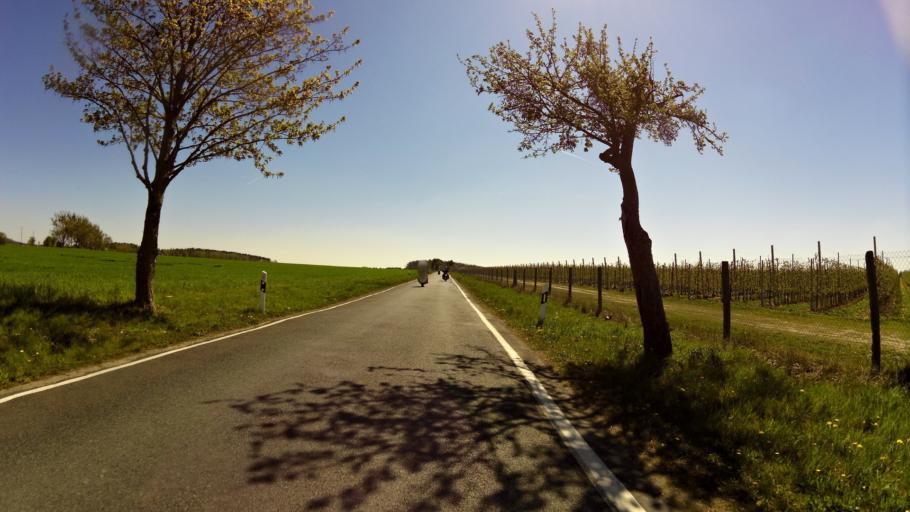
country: DE
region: Brandenburg
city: Werftpfuhl
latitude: 52.6338
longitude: 13.8060
